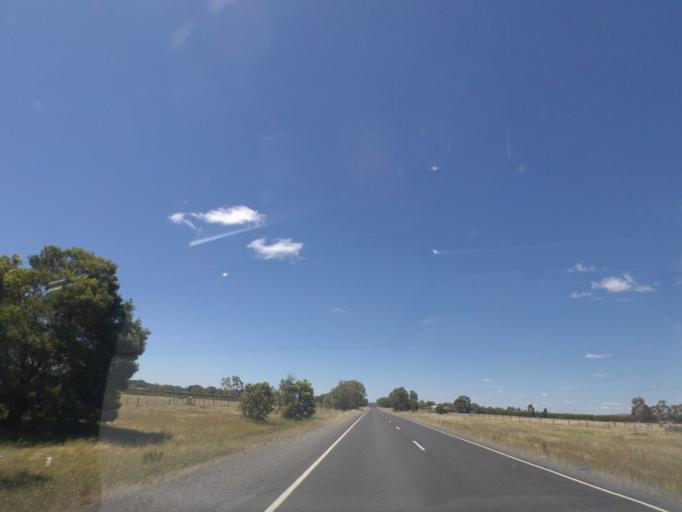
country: AU
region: Victoria
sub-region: Mount Alexander
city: Castlemaine
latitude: -37.2192
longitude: 144.3447
